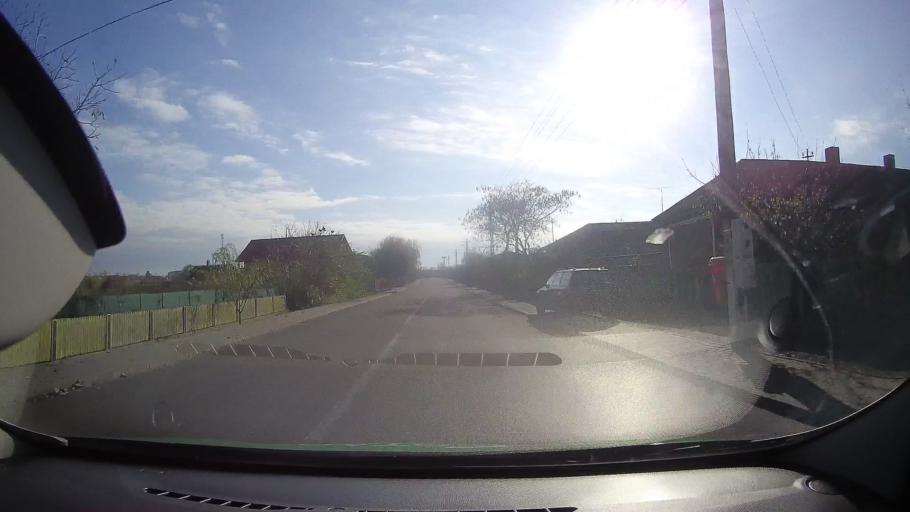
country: RO
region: Tulcea
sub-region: Comuna Murighiol
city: Murighiol
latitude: 45.0399
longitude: 29.1577
